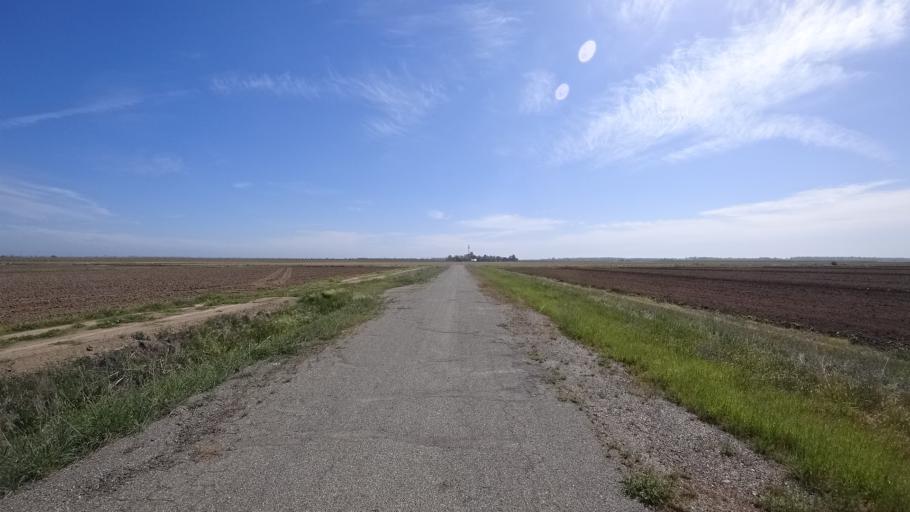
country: US
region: California
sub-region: Glenn County
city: Hamilton City
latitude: 39.6089
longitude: -122.0293
